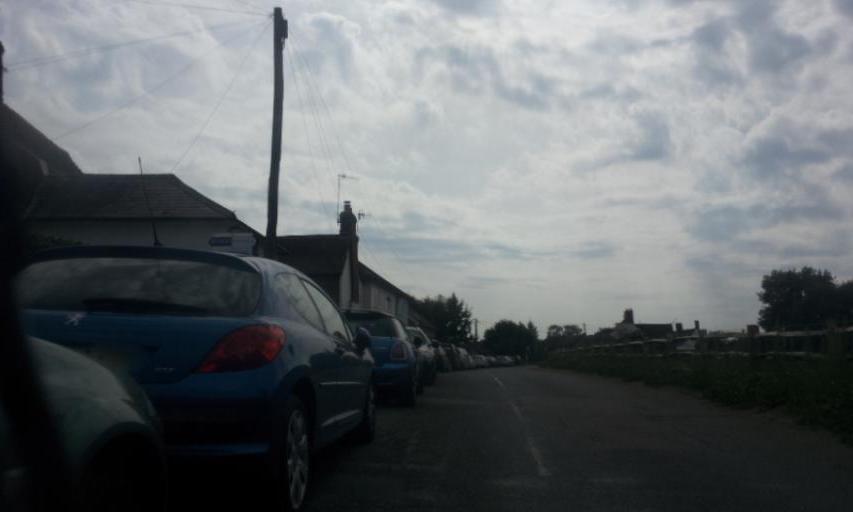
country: GB
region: England
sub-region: Kent
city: Yalding
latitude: 51.2088
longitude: 0.4190
